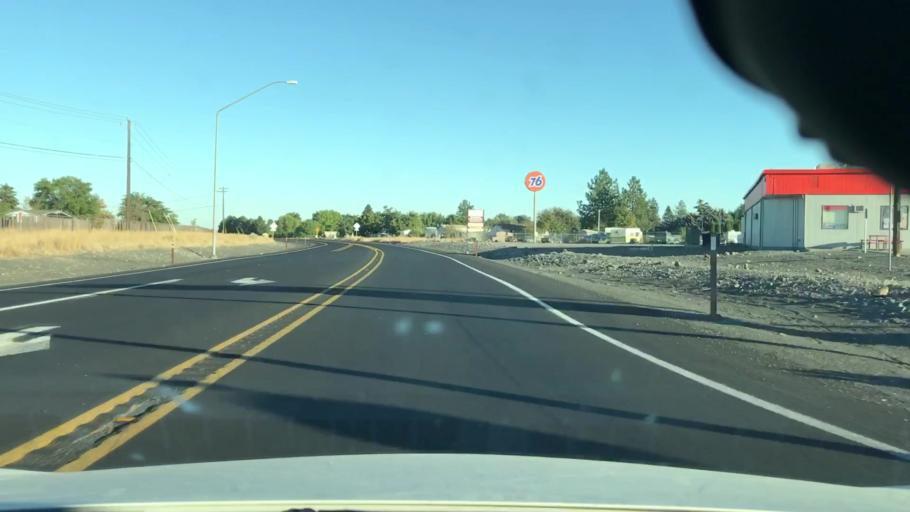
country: US
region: Washington
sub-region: Grant County
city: Cascade Valley
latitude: 47.1616
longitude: -119.3234
